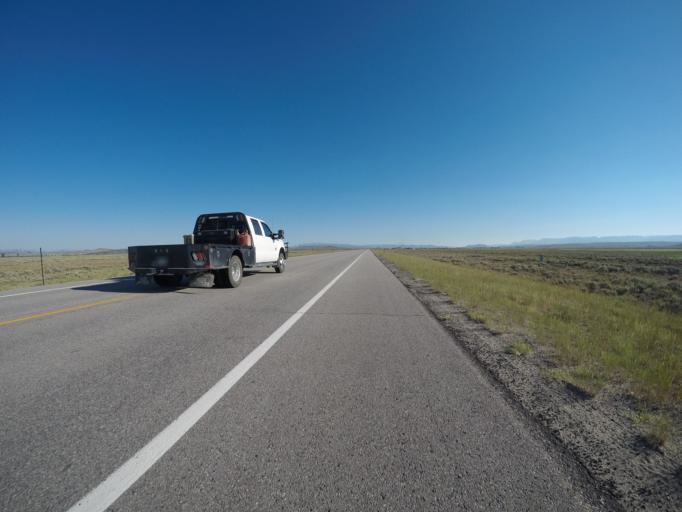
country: US
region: Wyoming
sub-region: Sublette County
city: Pinedale
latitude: 42.9598
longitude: -110.0877
